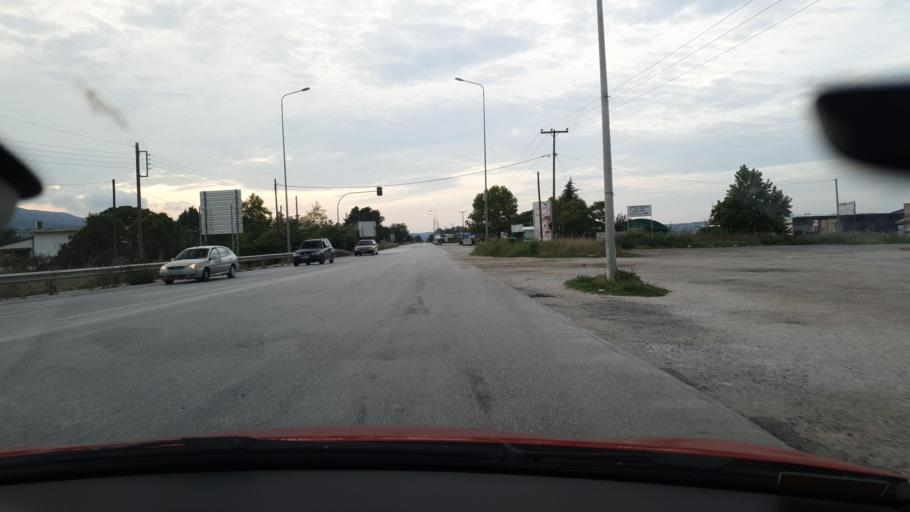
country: GR
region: Central Macedonia
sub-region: Nomos Thessalonikis
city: Liti
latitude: 40.7523
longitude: 22.9883
